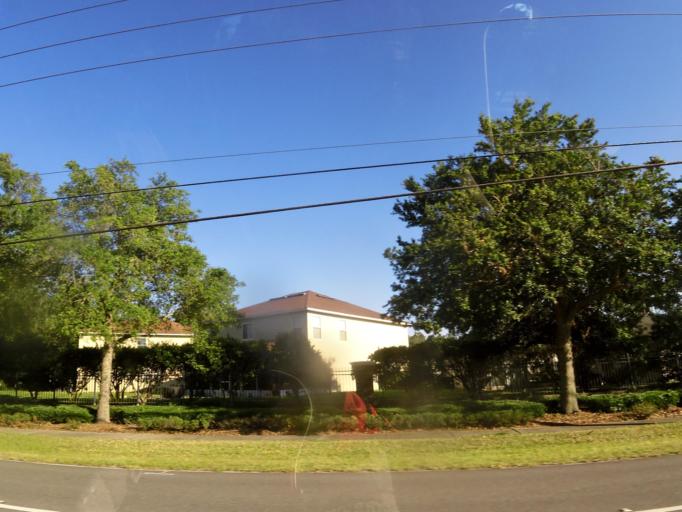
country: US
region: Florida
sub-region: Duval County
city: Jacksonville
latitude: 30.4647
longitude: -81.5545
